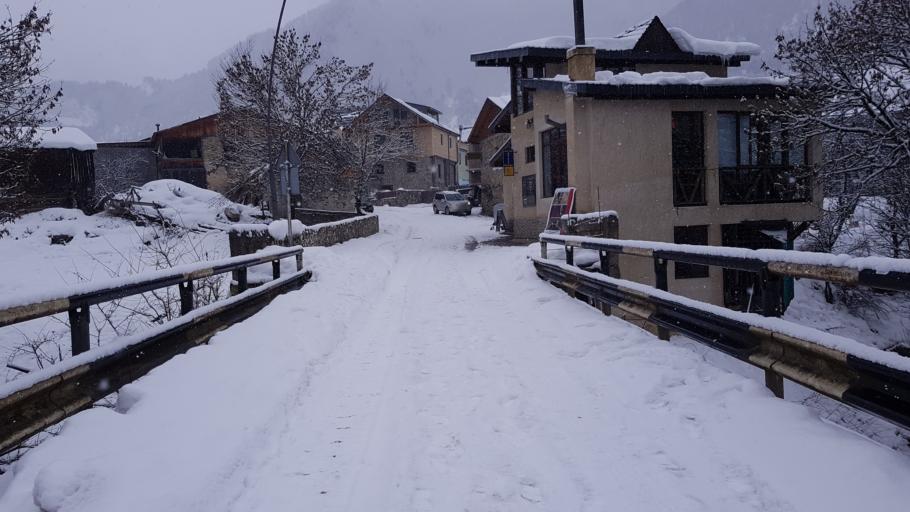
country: GE
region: Samegrelo and Zemo Svaneti
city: Mest'ia
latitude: 43.0426
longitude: 42.7278
